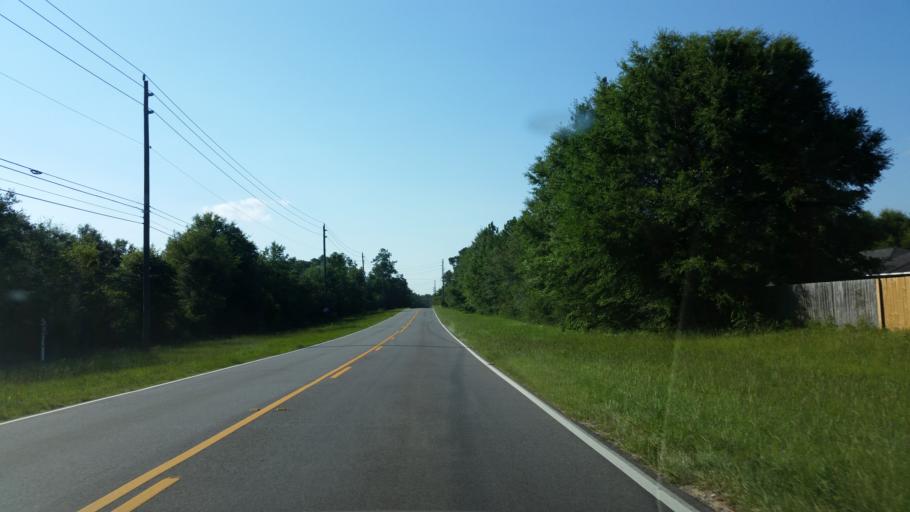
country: US
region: Florida
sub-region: Escambia County
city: Cantonment
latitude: 30.5627
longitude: -87.3849
